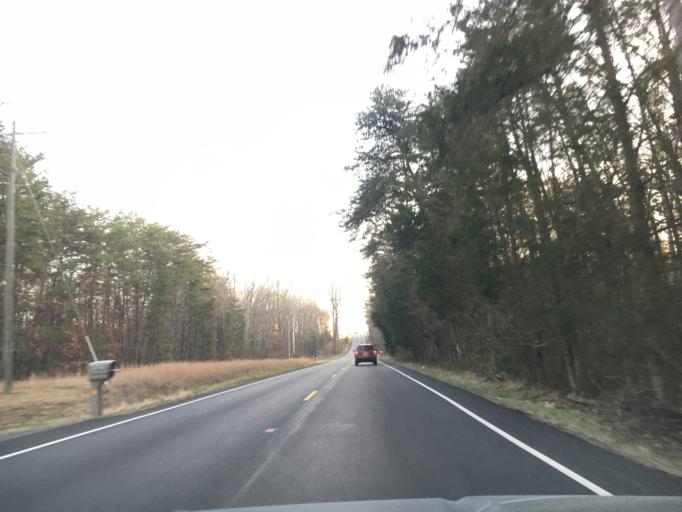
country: US
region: Virginia
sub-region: Orange County
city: Orange
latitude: 38.2347
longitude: -77.9503
